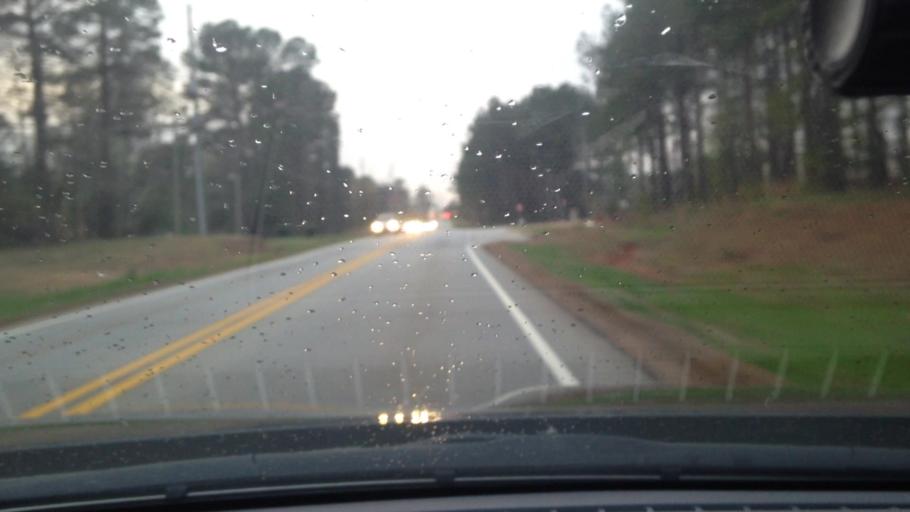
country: US
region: Georgia
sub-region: Coweta County
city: East Newnan
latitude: 33.3732
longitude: -84.7060
